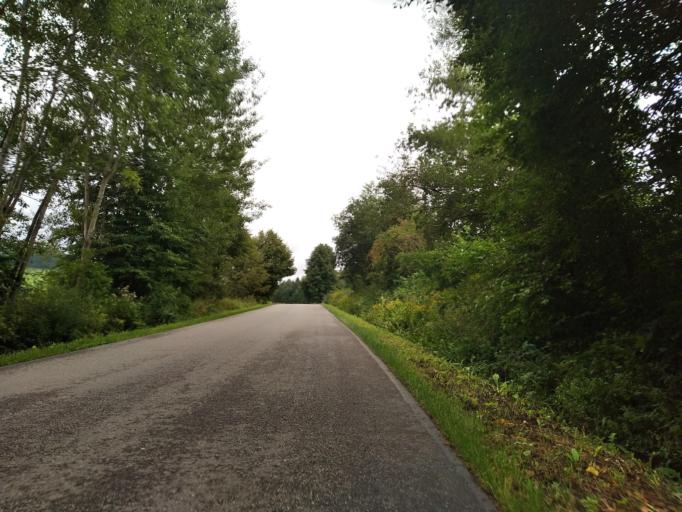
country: PL
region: Subcarpathian Voivodeship
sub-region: Powiat brzozowski
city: Nozdrzec
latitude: 49.7345
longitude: 22.2636
